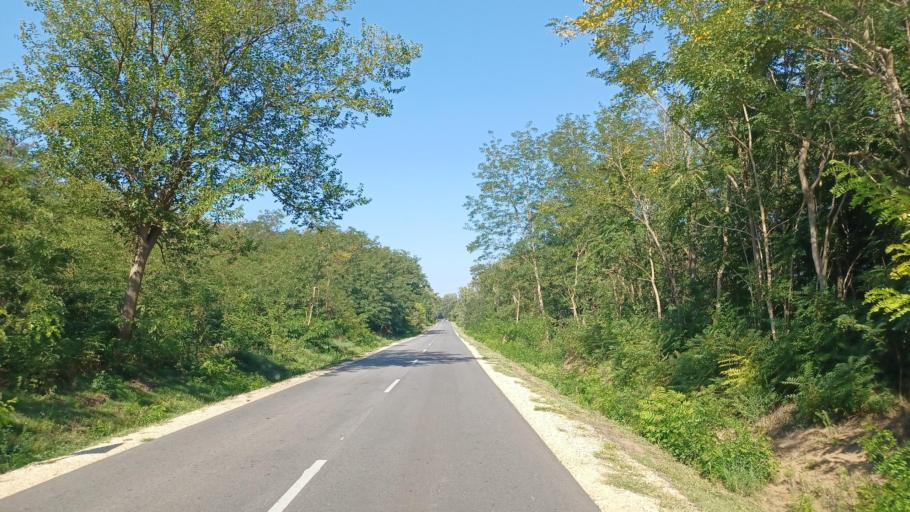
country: HU
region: Tolna
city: Nemetker
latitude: 46.7290
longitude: 18.7349
